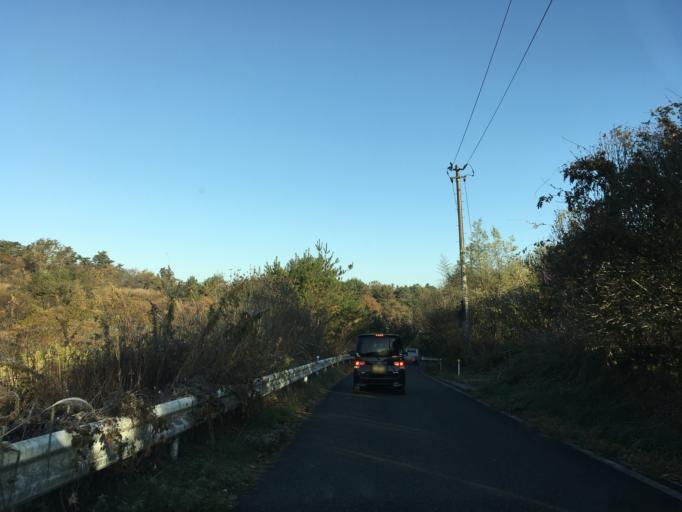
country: JP
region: Iwate
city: Ichinoseki
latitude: 38.7914
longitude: 141.2119
